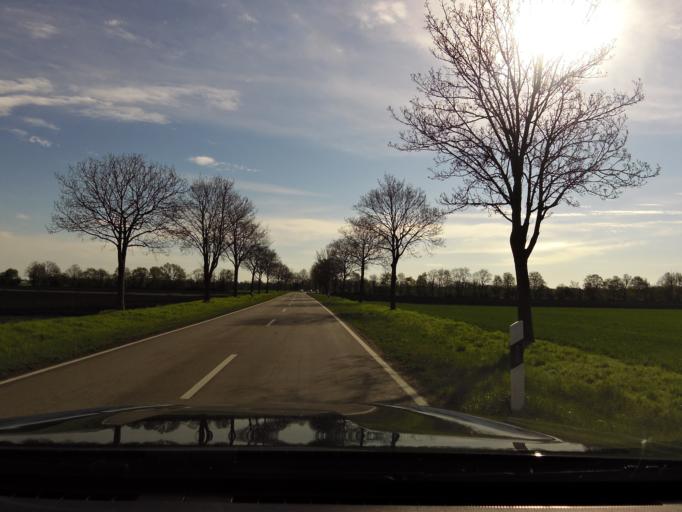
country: DE
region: Bavaria
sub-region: Upper Bavaria
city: Hallbergmoos
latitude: 48.3352
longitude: 11.7795
